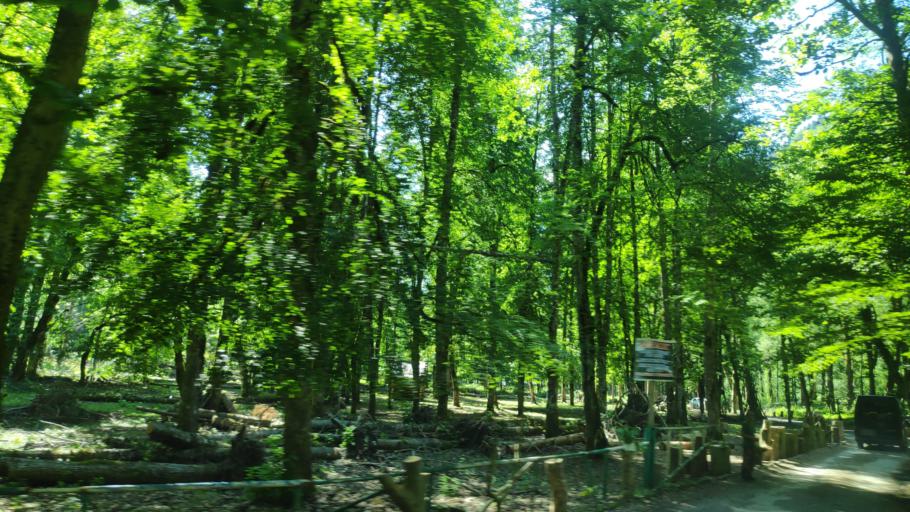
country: GE
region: Abkhazia
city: Gagra
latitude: 43.4810
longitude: 40.5627
